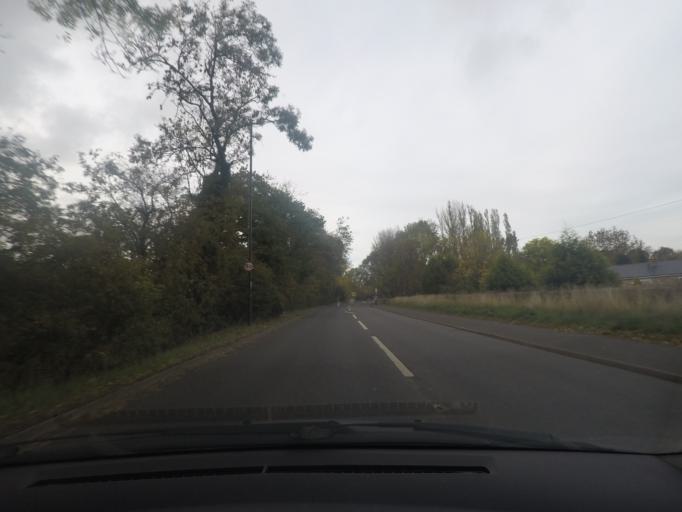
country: GB
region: England
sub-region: Sheffield
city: Chapletown
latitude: 53.4531
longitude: -1.4939
